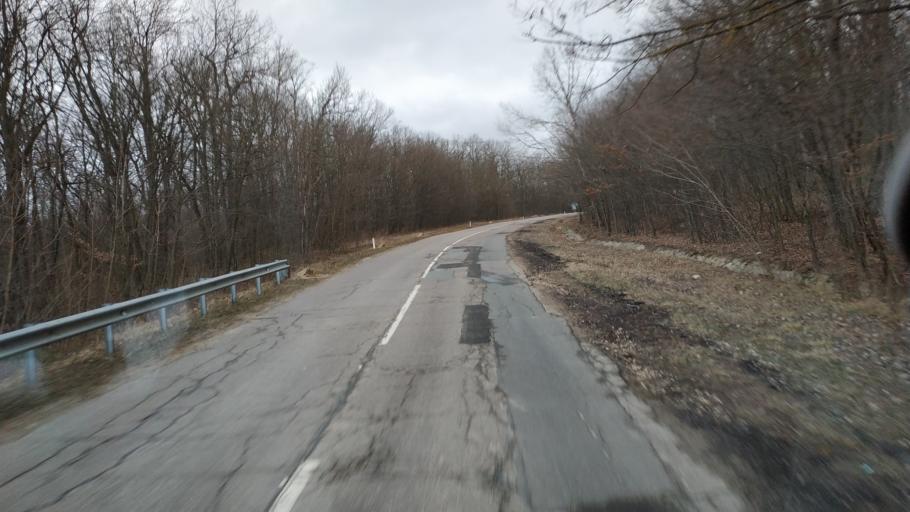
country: MD
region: Calarasi
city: Calarasi
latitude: 47.2393
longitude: 28.2802
